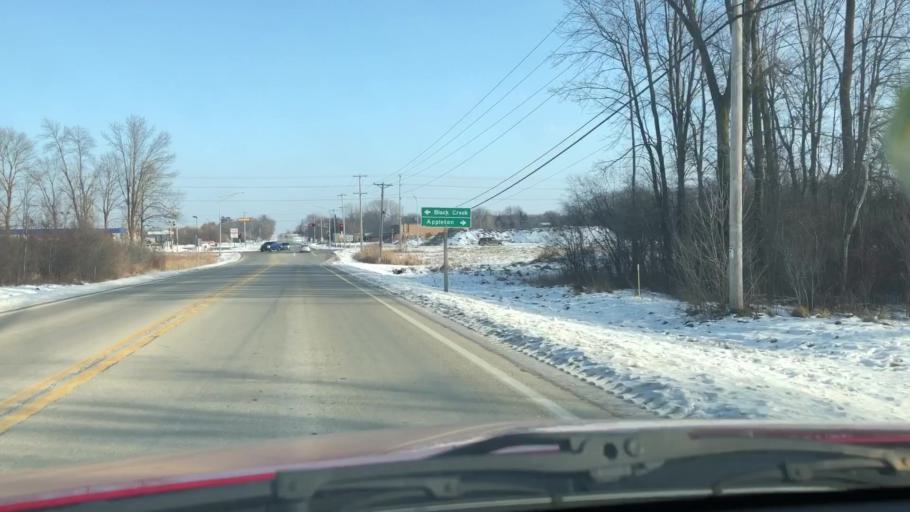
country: US
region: Wisconsin
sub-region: Outagamie County
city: Appleton
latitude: 44.3165
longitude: -88.4169
